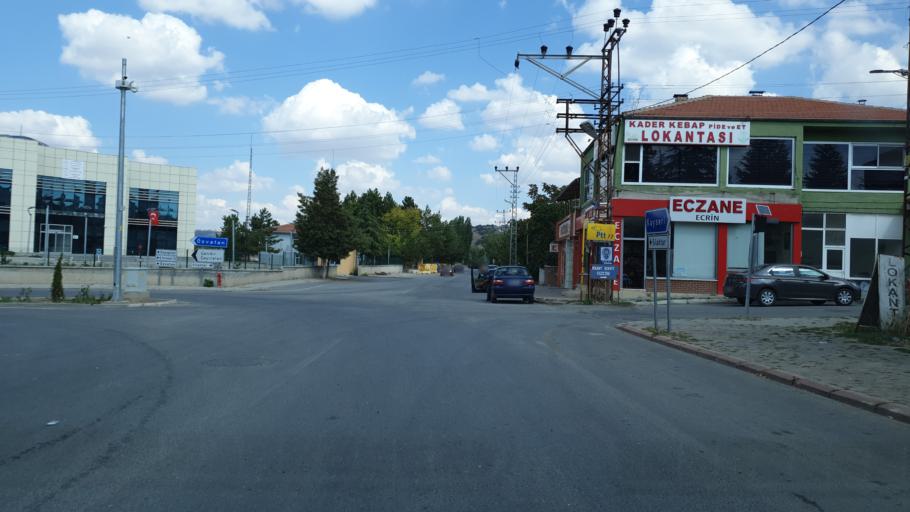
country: TR
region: Kayseri
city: Felahiye
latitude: 39.0905
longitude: 35.5693
